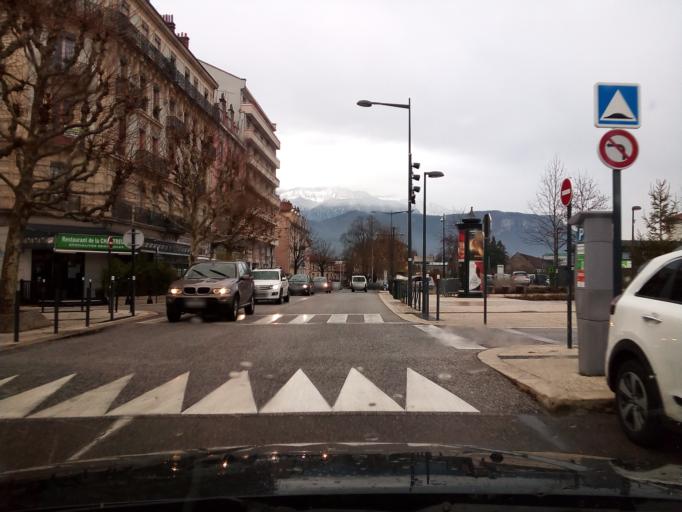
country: FR
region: Rhone-Alpes
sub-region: Departement de l'Isere
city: Voiron
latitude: 45.3644
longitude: 5.5950
